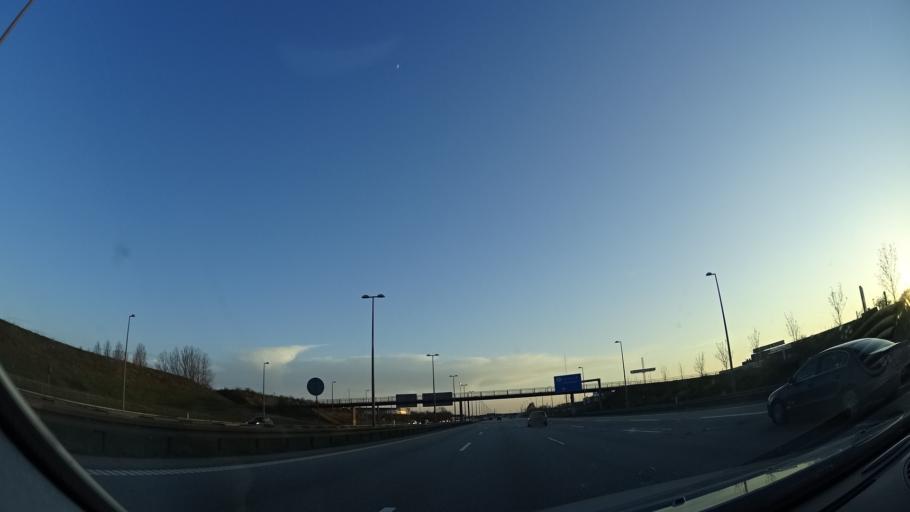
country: DK
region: Zealand
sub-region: Greve Kommune
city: Greve
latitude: 55.6070
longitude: 12.3117
